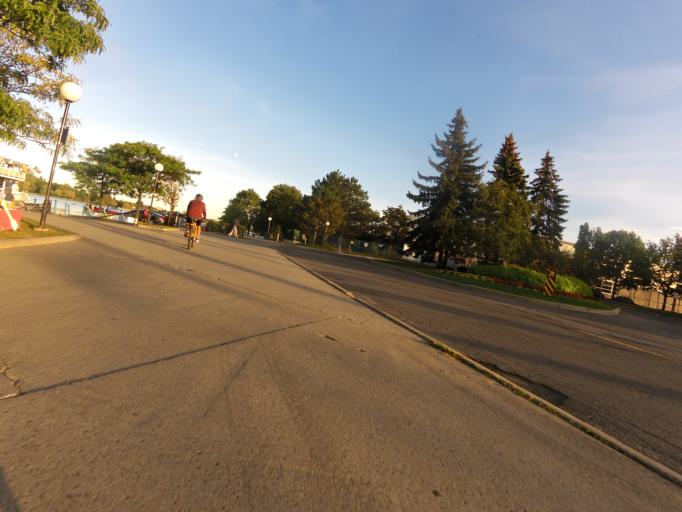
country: CA
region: Ontario
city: Ottawa
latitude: 45.3961
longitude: -75.7065
